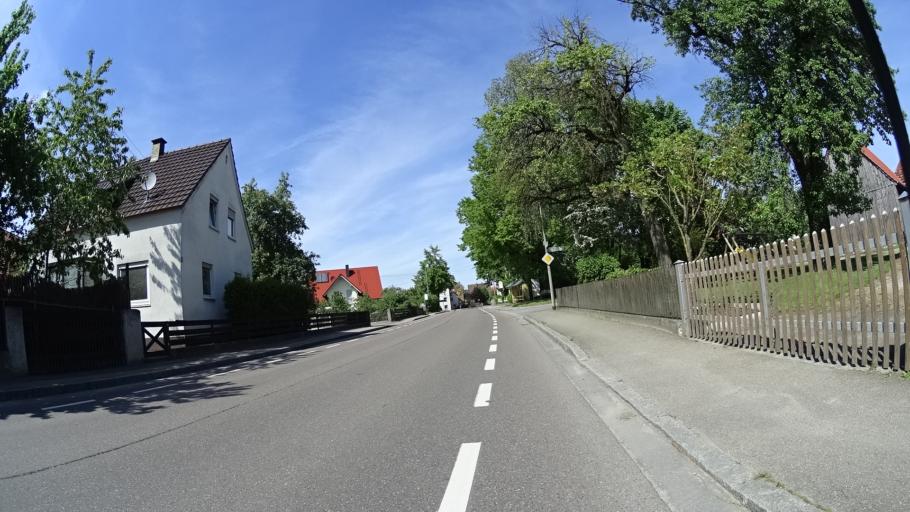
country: DE
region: Bavaria
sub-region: Swabia
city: Weissenhorn
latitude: 48.3274
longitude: 10.1603
